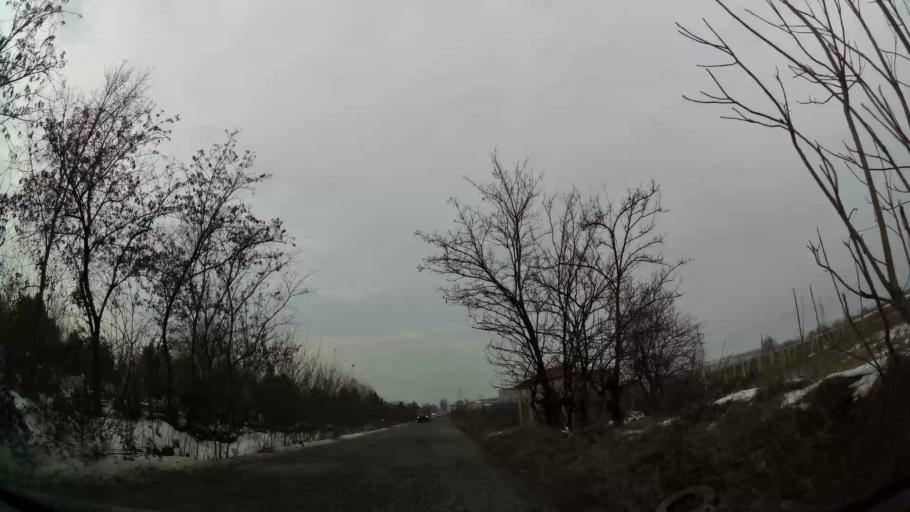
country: MK
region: Suto Orizari
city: Suto Orizare
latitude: 42.0437
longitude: 21.4356
